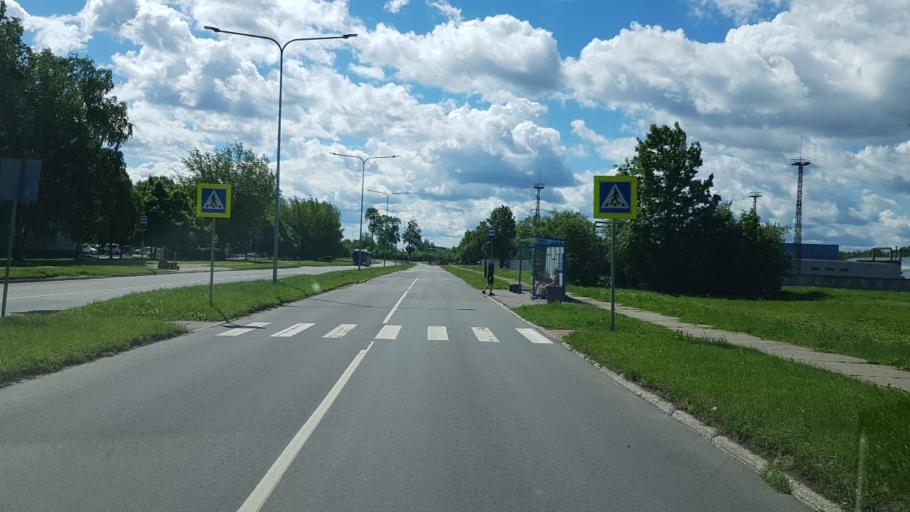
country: EE
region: Ida-Virumaa
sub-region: Narva linn
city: Narva
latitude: 59.3611
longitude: 28.1874
